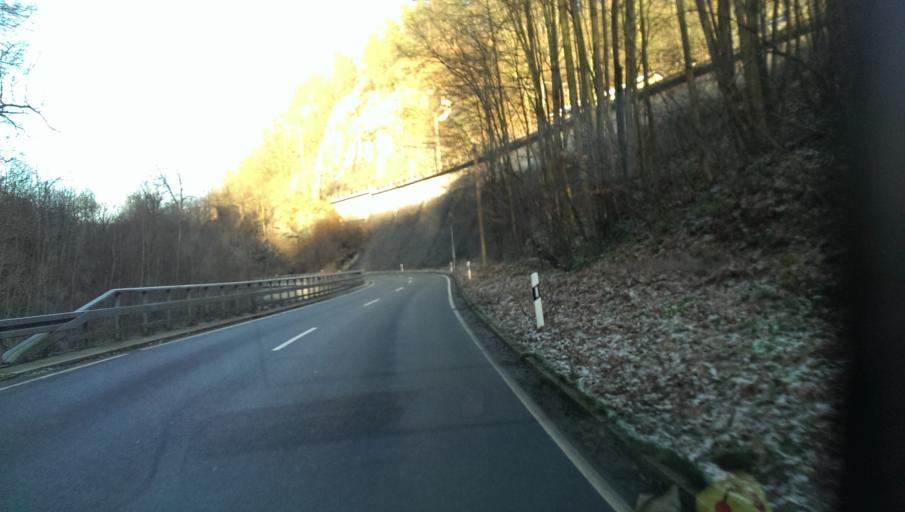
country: DE
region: Saxony
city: Dorfhain
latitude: 50.9501
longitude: 13.5827
